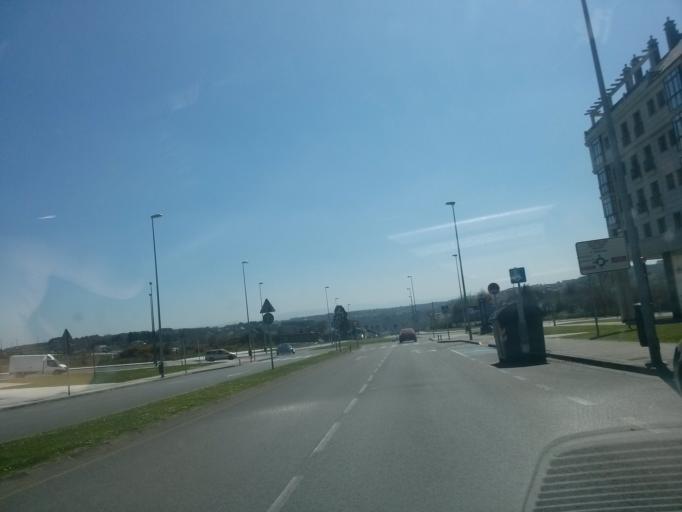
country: ES
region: Galicia
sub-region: Provincia de Lugo
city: Lugo
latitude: 42.9974
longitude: -7.5459
